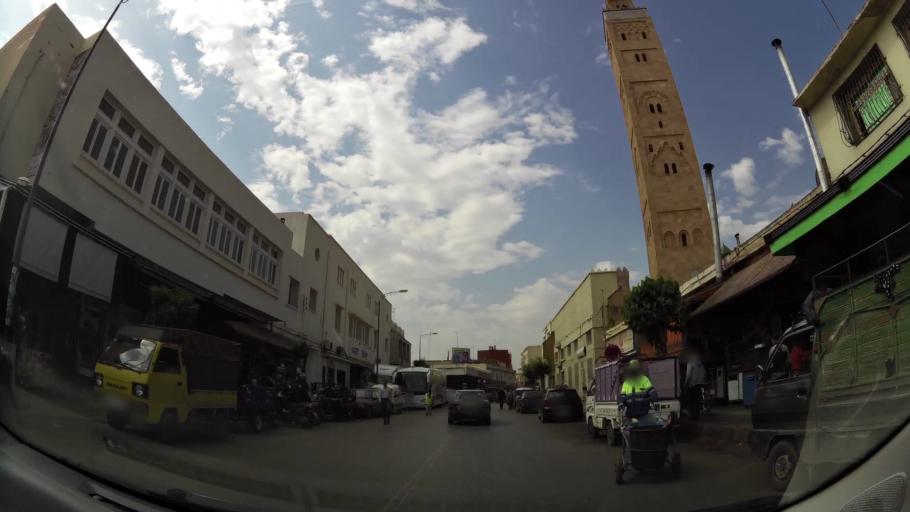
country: MA
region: Oriental
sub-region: Oujda-Angad
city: Oujda
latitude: 34.6836
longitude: -1.9143
